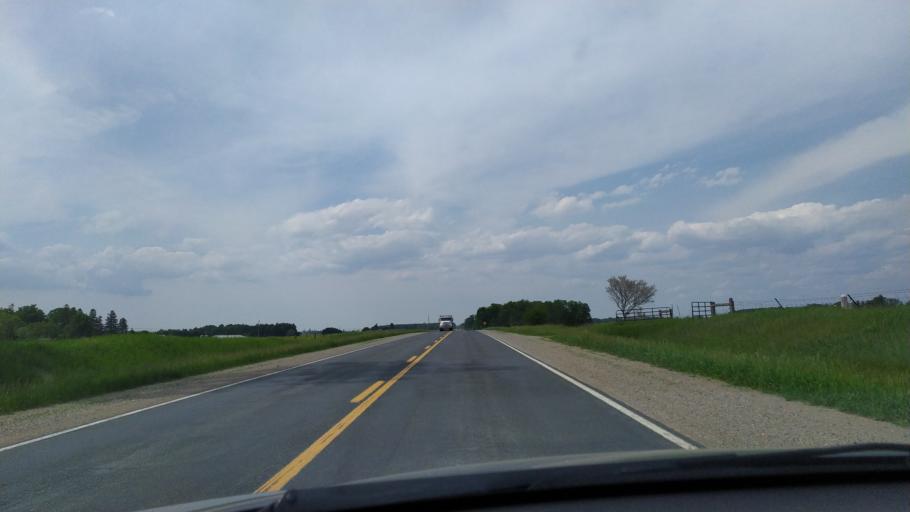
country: CA
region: Ontario
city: Ingersoll
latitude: 43.0233
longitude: -80.9695
